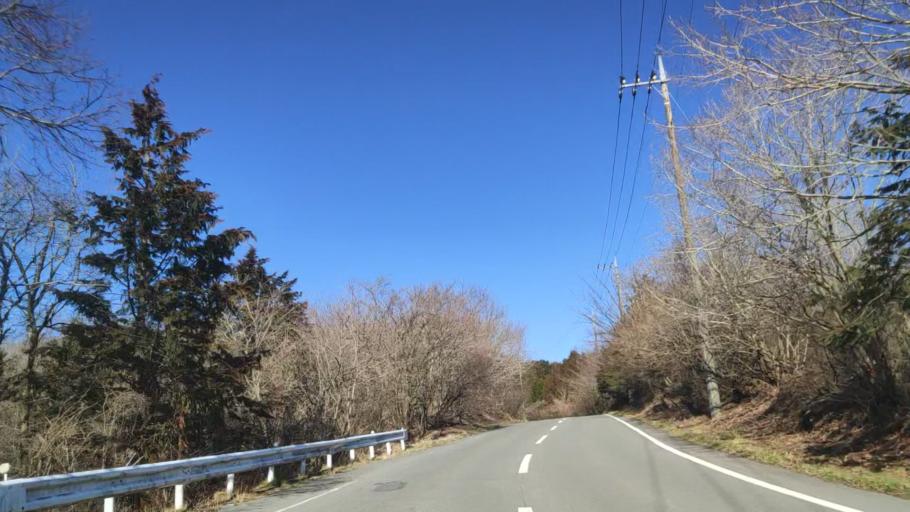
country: JP
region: Yamanashi
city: Fujikawaguchiko
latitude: 35.3854
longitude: 138.6062
